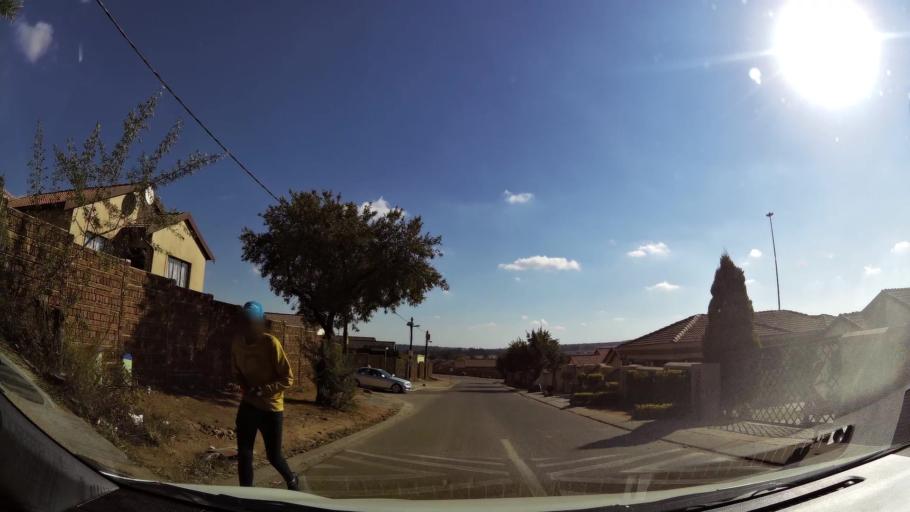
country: ZA
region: Gauteng
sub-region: City of Tshwane Metropolitan Municipality
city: Cullinan
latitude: -25.6908
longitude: 28.4156
